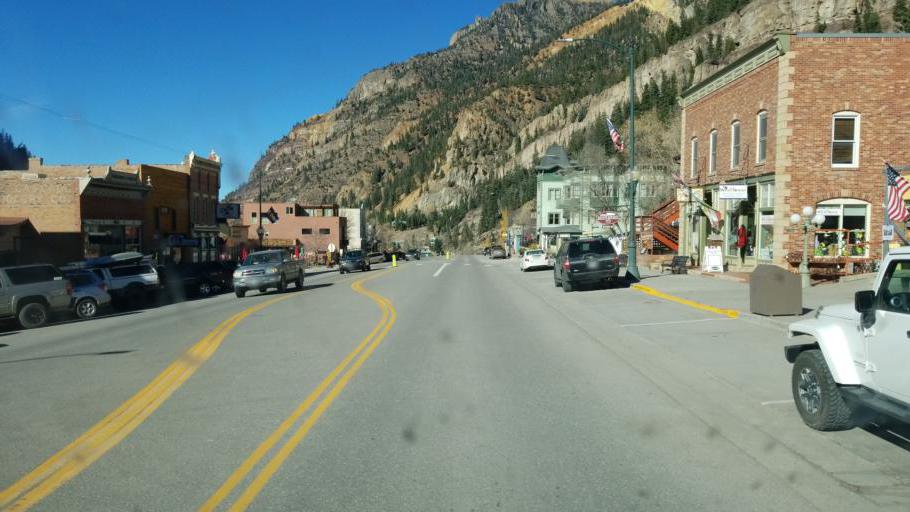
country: US
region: Colorado
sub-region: Ouray County
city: Ouray
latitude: 38.0243
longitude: -107.6714
